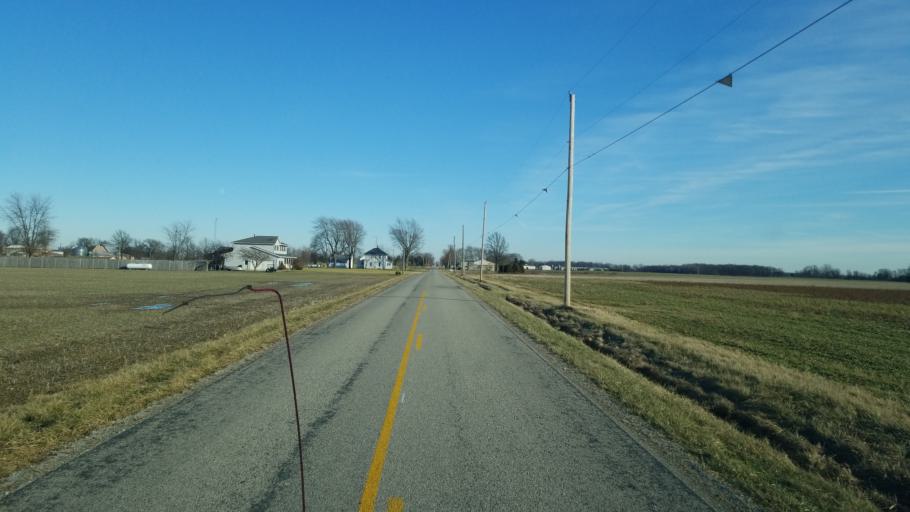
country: US
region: Ohio
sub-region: Sandusky County
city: Mount Carmel
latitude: 41.2560
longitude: -82.9455
